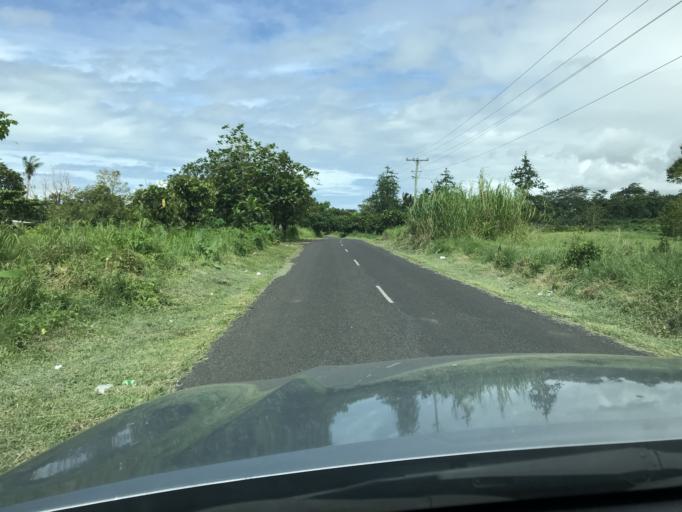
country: WS
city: Fasito`outa
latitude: -13.8589
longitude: -171.9059
